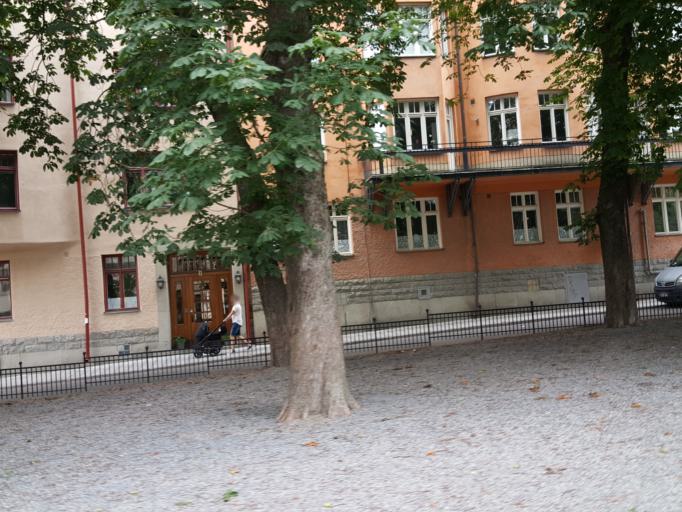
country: SE
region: Stockholm
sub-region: Stockholms Kommun
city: Stockholm
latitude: 59.3277
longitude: 18.0465
